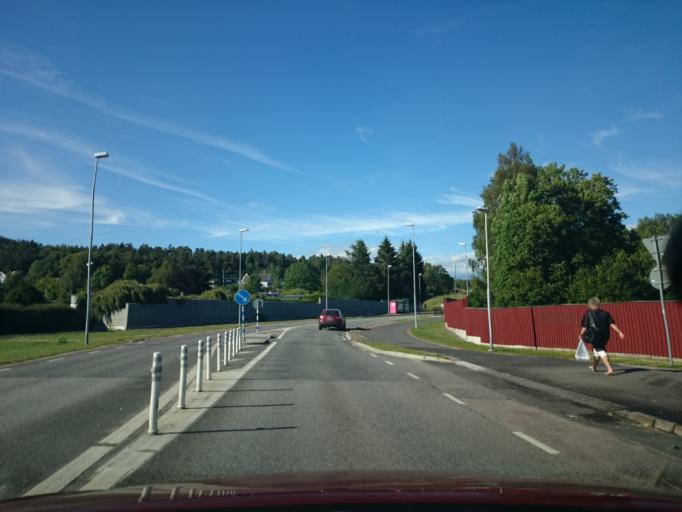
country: SE
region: Vaestra Goetaland
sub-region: Lerums Kommun
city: Lerum
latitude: 57.7765
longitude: 12.2772
